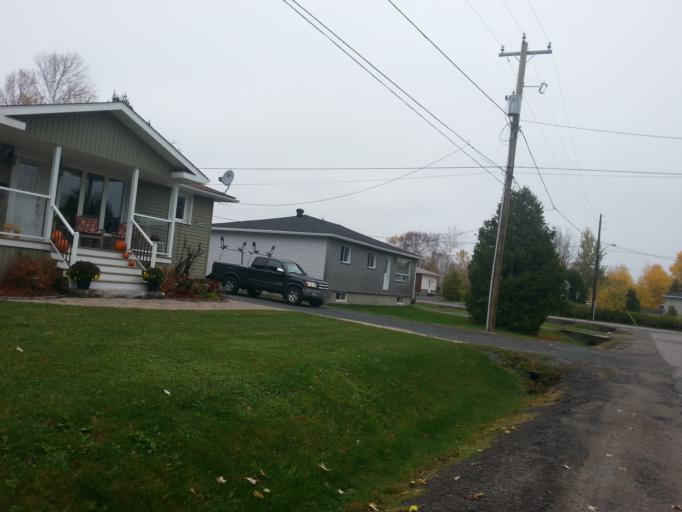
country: CA
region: Ontario
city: Greater Sudbury
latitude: 46.5437
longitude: -81.0981
